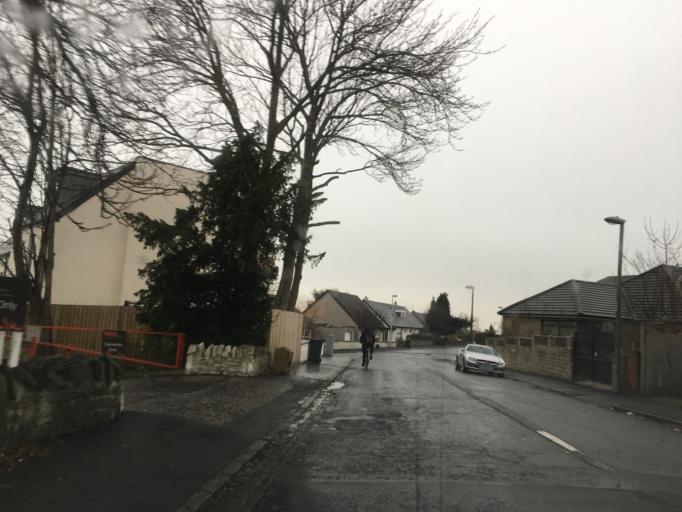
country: GB
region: Scotland
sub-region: Edinburgh
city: Currie
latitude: 55.9478
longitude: -3.2949
